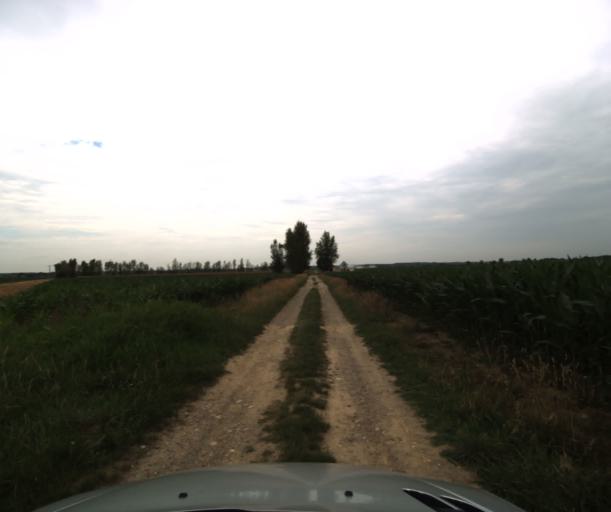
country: FR
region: Midi-Pyrenees
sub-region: Departement de la Haute-Garonne
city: Lacasse
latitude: 43.4286
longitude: 1.2672
